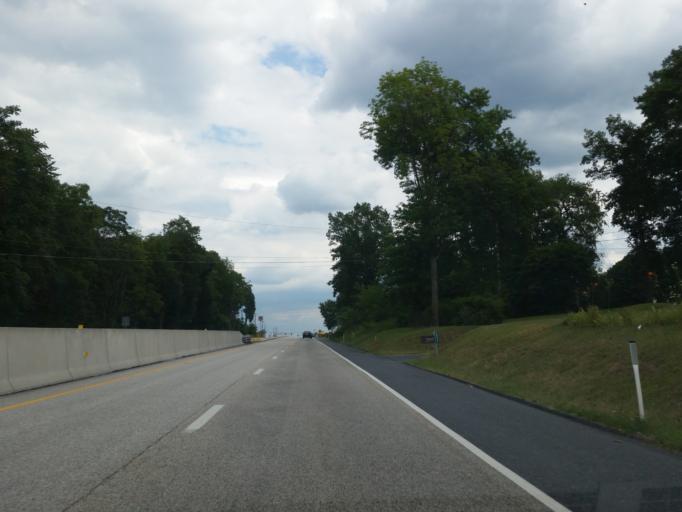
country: US
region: Pennsylvania
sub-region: Lebanon County
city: Jonestown
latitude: 40.4063
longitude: -76.5413
